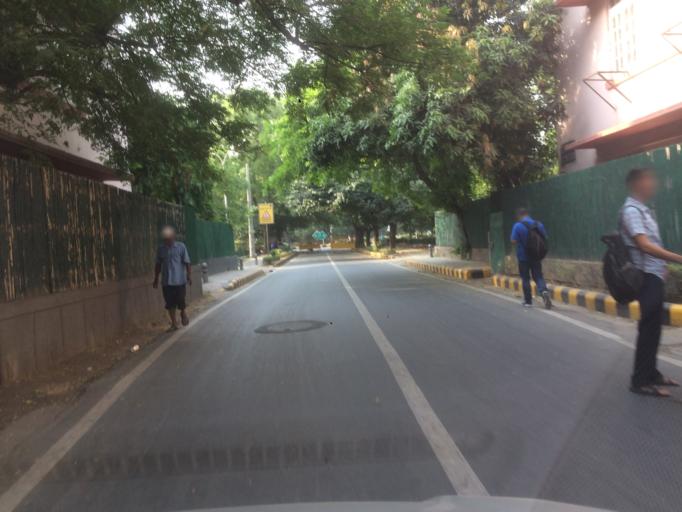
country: IN
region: NCT
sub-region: Central Delhi
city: Karol Bagh
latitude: 28.5804
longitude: 77.1777
